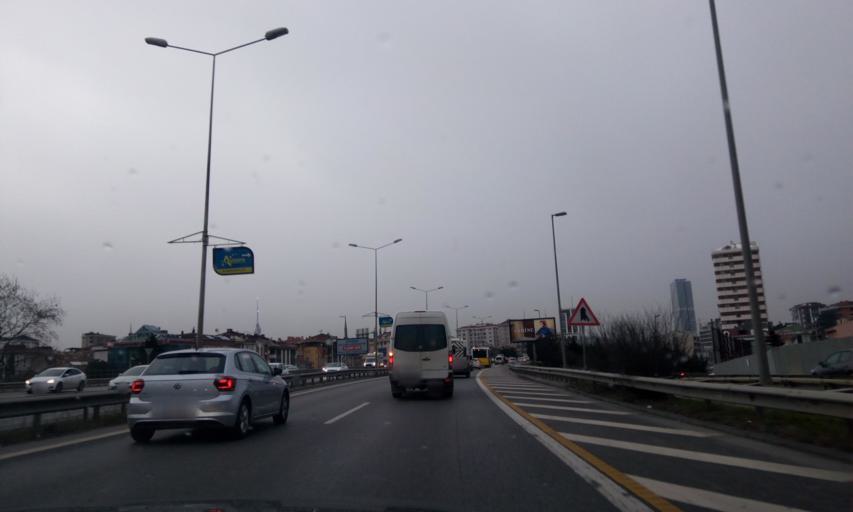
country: TR
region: Istanbul
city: Umraniye
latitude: 41.0291
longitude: 29.1082
